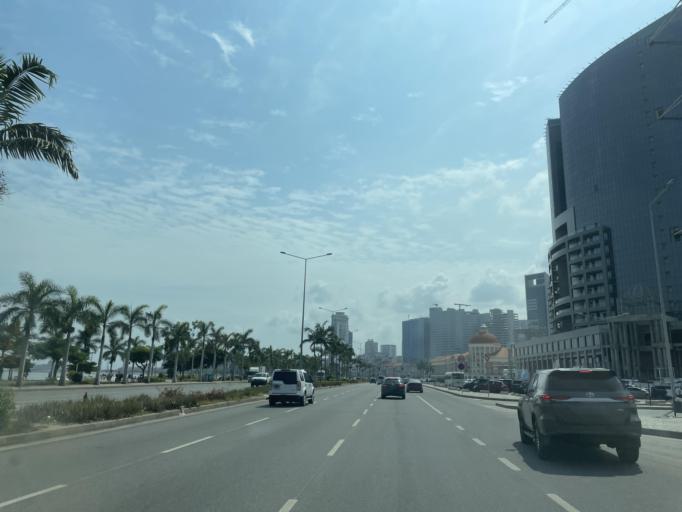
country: AO
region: Luanda
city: Luanda
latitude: -8.8107
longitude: 13.2308
